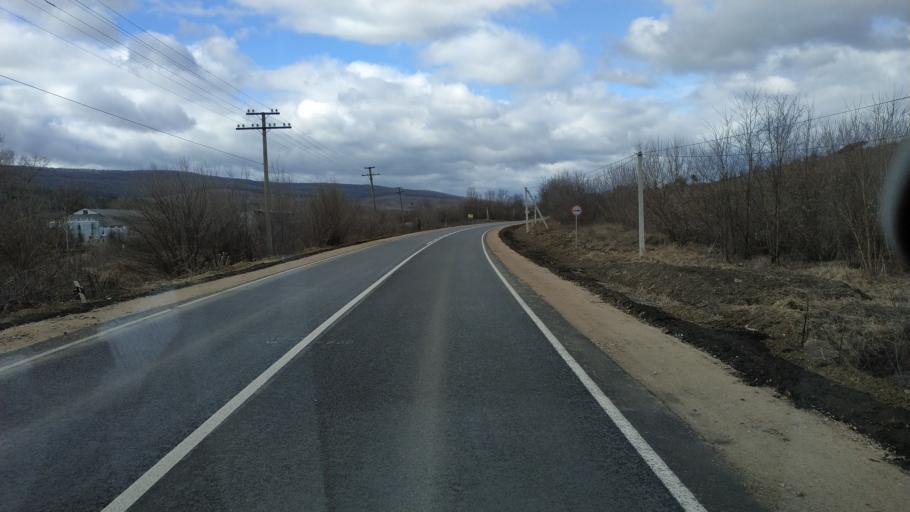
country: MD
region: Stinga Nistrului
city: Bucovat
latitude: 47.1904
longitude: 28.4450
